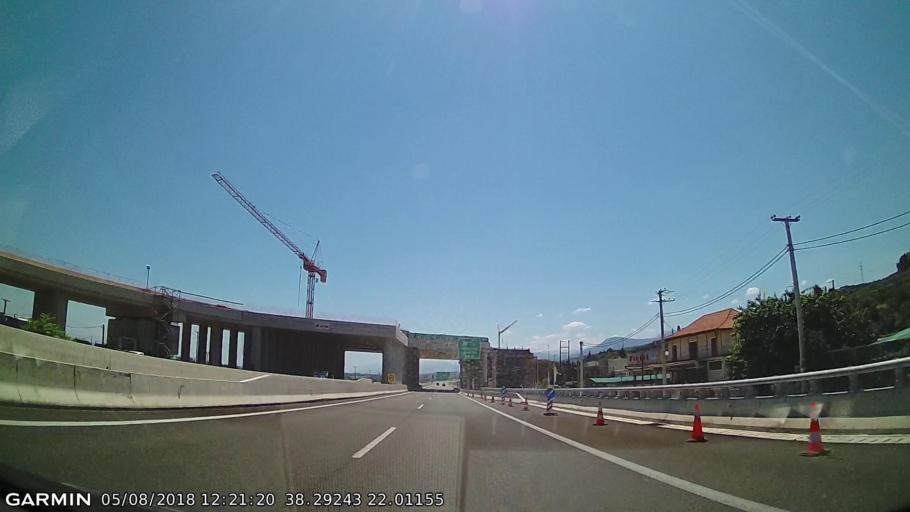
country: GR
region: West Greece
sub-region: Nomos Achaias
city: Kamarai
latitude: 38.2923
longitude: 22.0118
